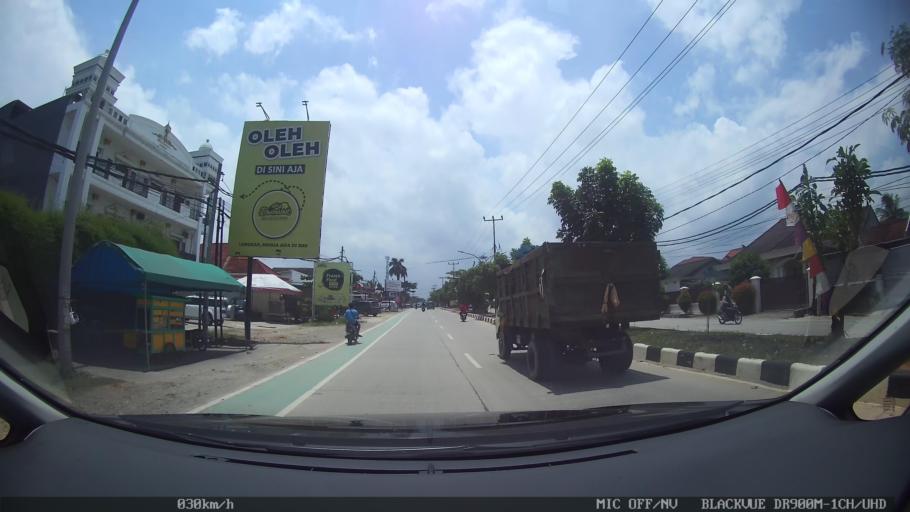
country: ID
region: Lampung
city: Kedaton
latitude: -5.3689
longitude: 105.2993
